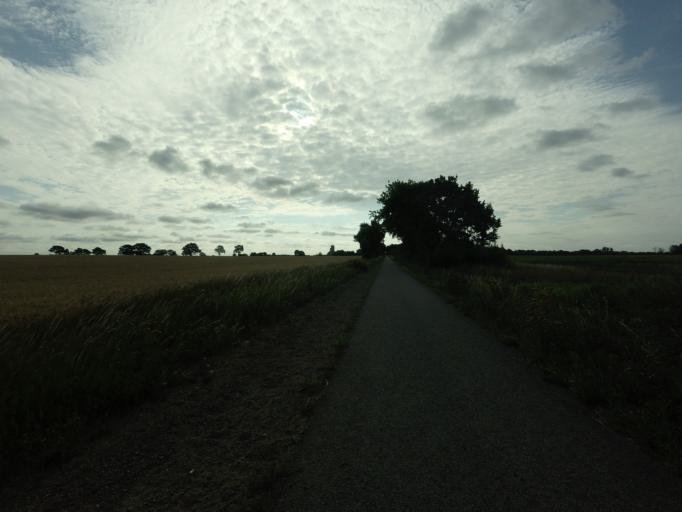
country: SE
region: Skane
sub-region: Hoganas Kommun
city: Hoganas
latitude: 56.1803
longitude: 12.6629
